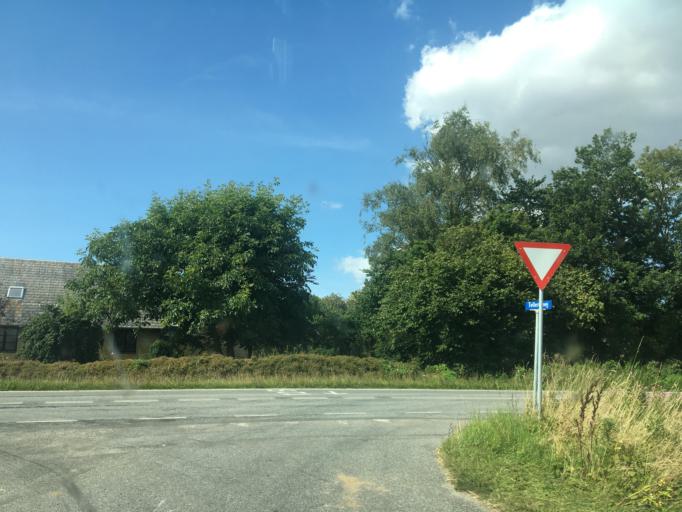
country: DK
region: South Denmark
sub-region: Middelfart Kommune
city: Ejby
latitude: 55.4066
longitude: 9.9125
